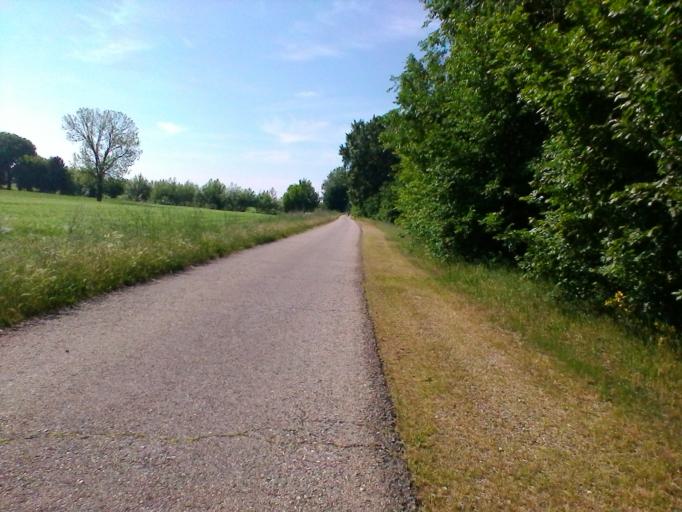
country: IT
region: Lombardy
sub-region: Provincia di Mantova
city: Marmirolo
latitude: 45.2339
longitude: 10.7281
